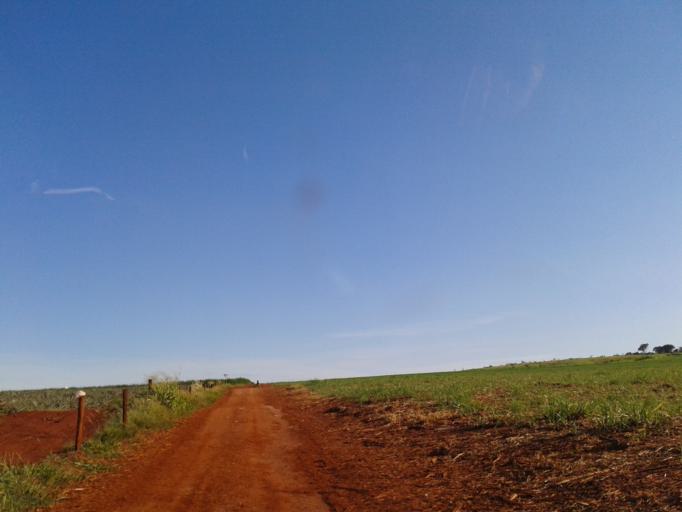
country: BR
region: Minas Gerais
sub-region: Centralina
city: Centralina
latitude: -18.6741
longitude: -49.2720
